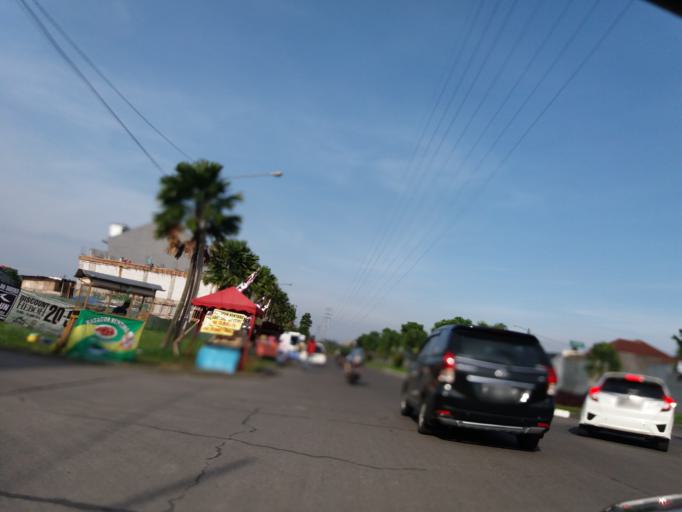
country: ID
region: West Java
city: Bandung
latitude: -6.9547
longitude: 107.6313
